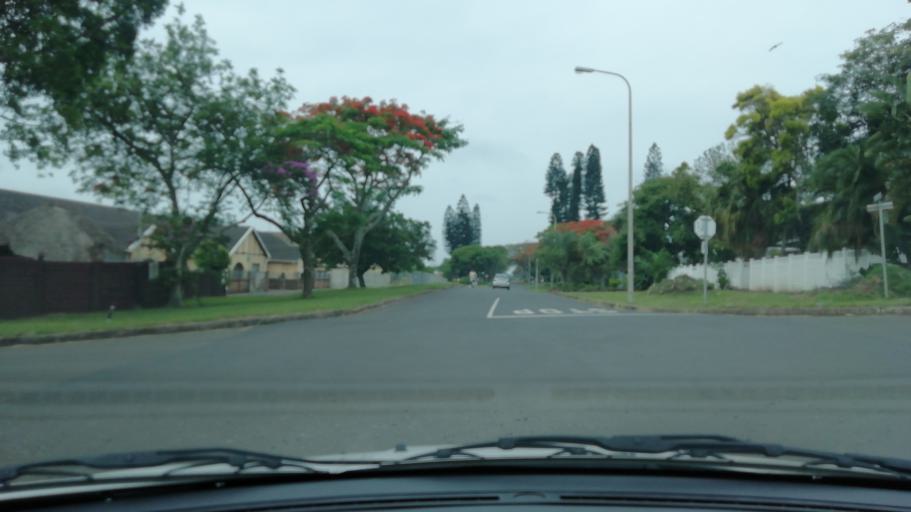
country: ZA
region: KwaZulu-Natal
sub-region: uThungulu District Municipality
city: Empangeni
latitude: -28.7405
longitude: 31.8875
